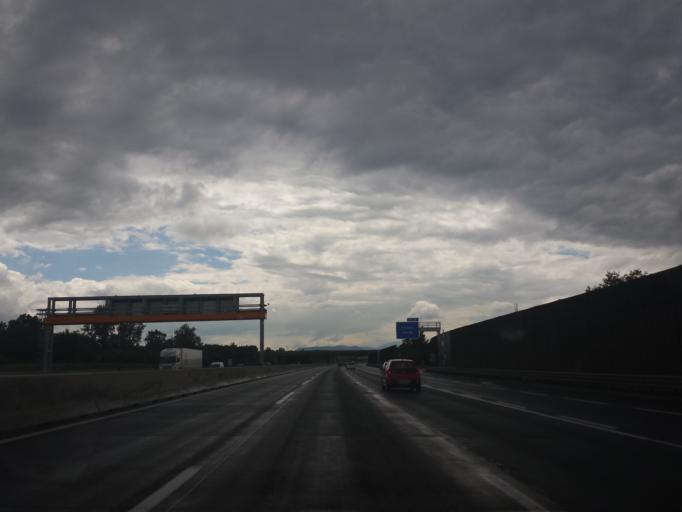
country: AT
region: Lower Austria
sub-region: Politischer Bezirk Baden
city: Traiskirchen
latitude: 47.9886
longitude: 16.2812
